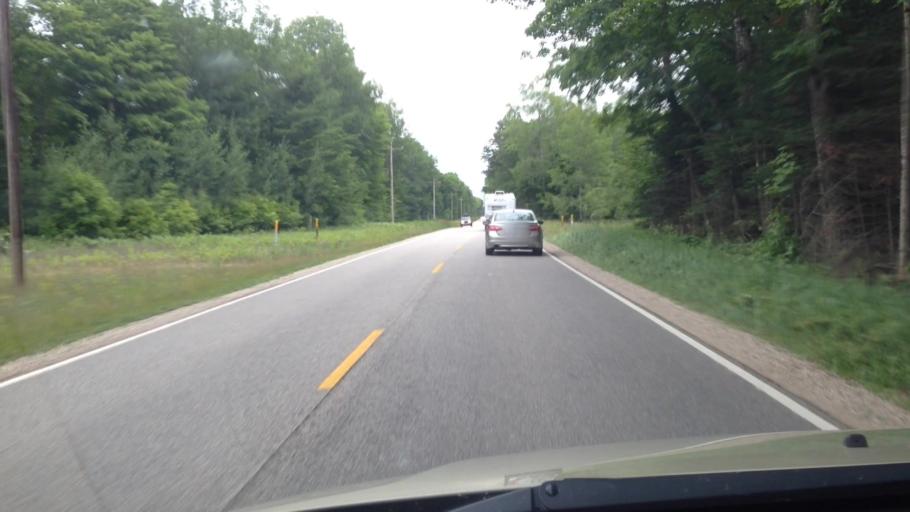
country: US
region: Michigan
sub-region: Mackinac County
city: Saint Ignace
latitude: 46.0568
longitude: -85.1423
